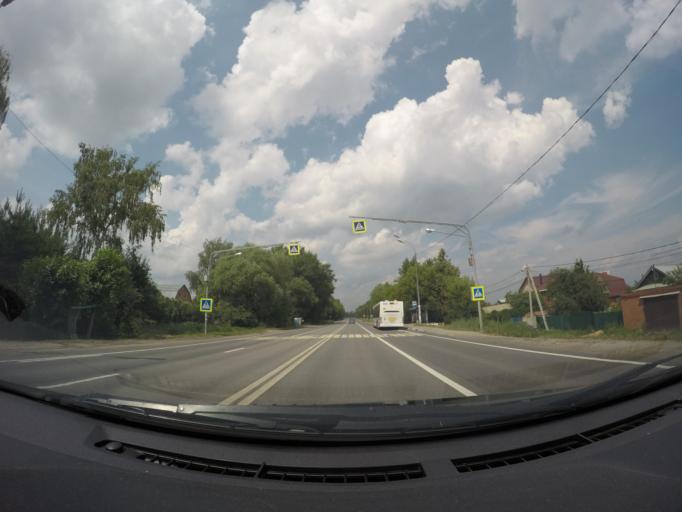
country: RU
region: Moskovskaya
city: Bronnitsy
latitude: 55.4620
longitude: 38.2010
